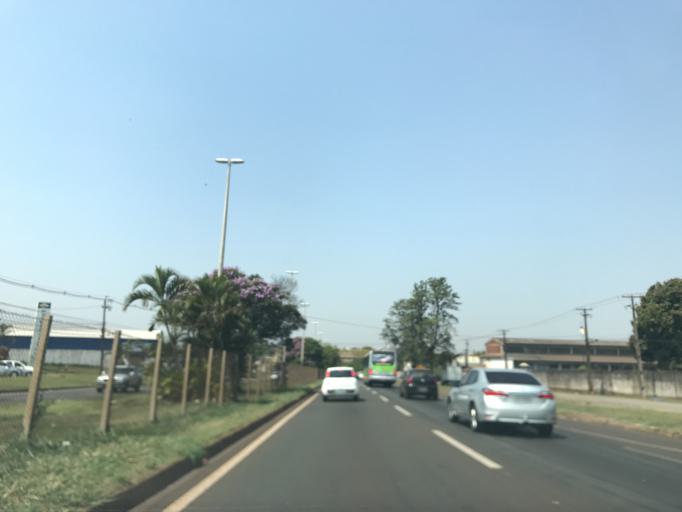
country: BR
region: Parana
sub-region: Cambe
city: Cambe
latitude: -23.2848
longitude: -51.2415
